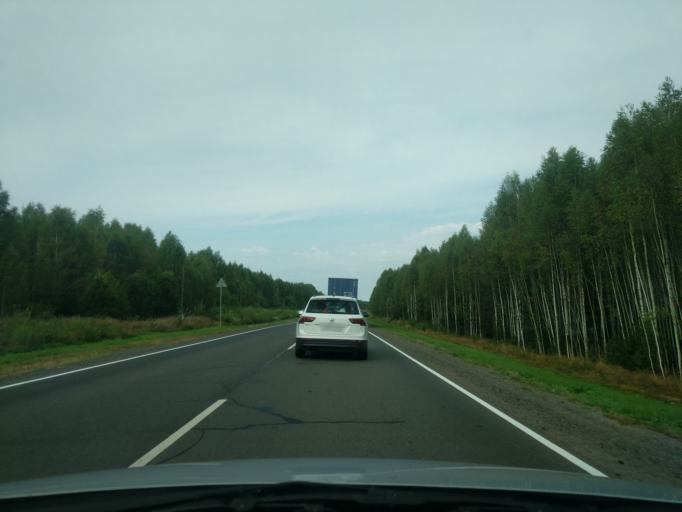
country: RU
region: Kirov
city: Leninskoye
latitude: 58.2844
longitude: 47.2599
